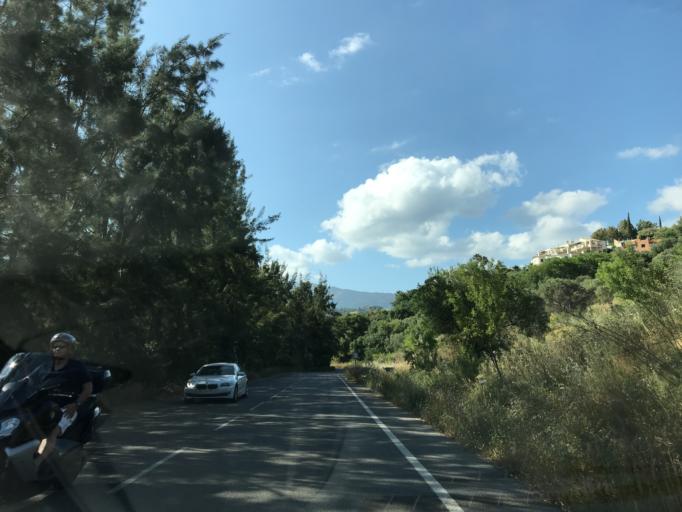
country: ES
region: Andalusia
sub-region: Provincia de Malaga
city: Benahavis
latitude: 36.5053
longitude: -5.0137
